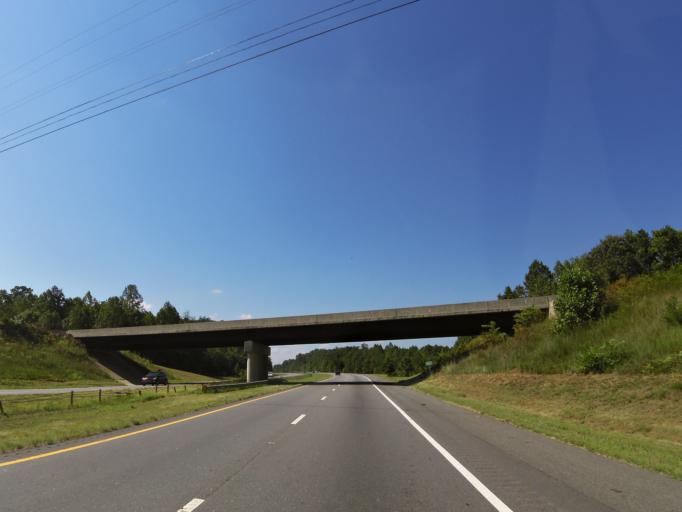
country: US
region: North Carolina
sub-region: Catawba County
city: Mountain View
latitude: 35.6563
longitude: -81.3172
